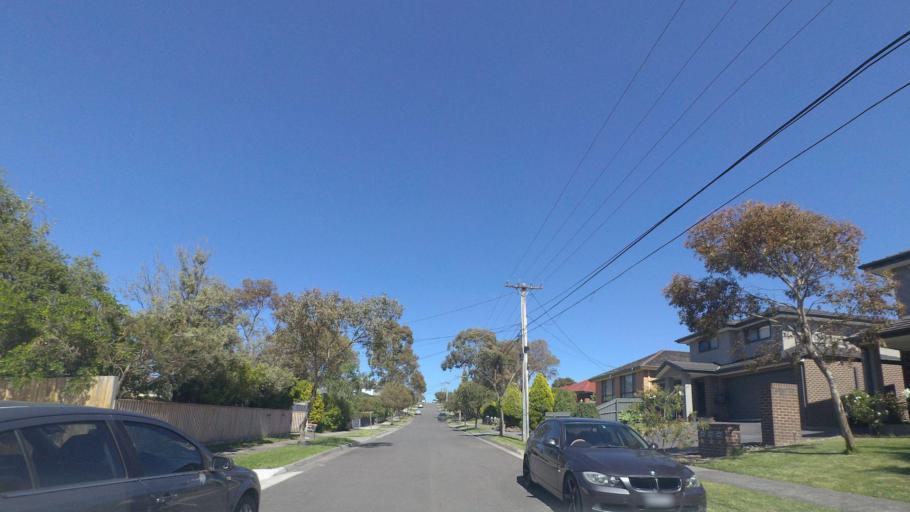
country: AU
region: Victoria
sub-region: Knox
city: Ferntree Gully
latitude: -37.8850
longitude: 145.2786
